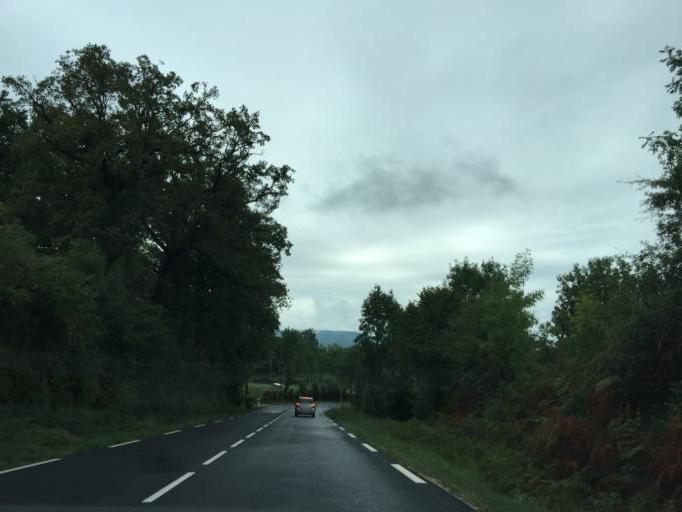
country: FR
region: Midi-Pyrenees
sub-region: Departement de l'Aveyron
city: Espalion
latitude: 44.5456
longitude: 2.7779
